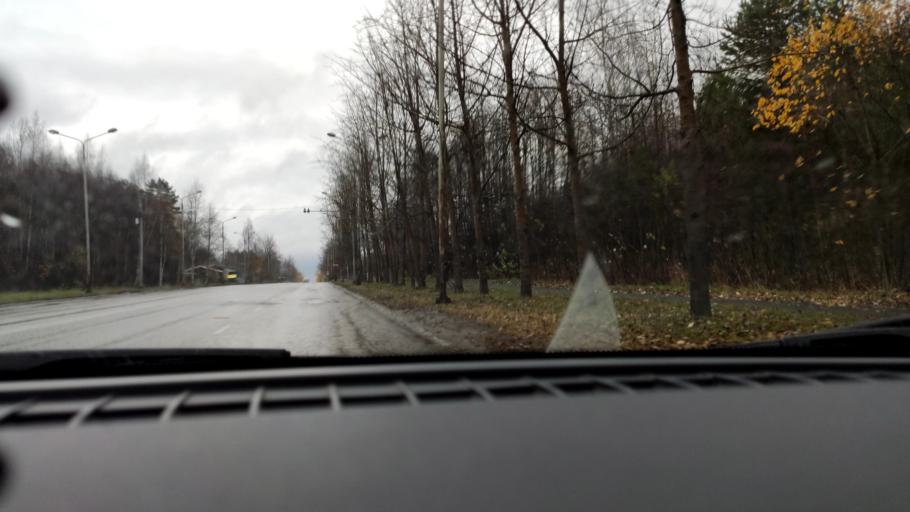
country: RU
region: Perm
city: Perm
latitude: 58.0772
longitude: 56.3709
